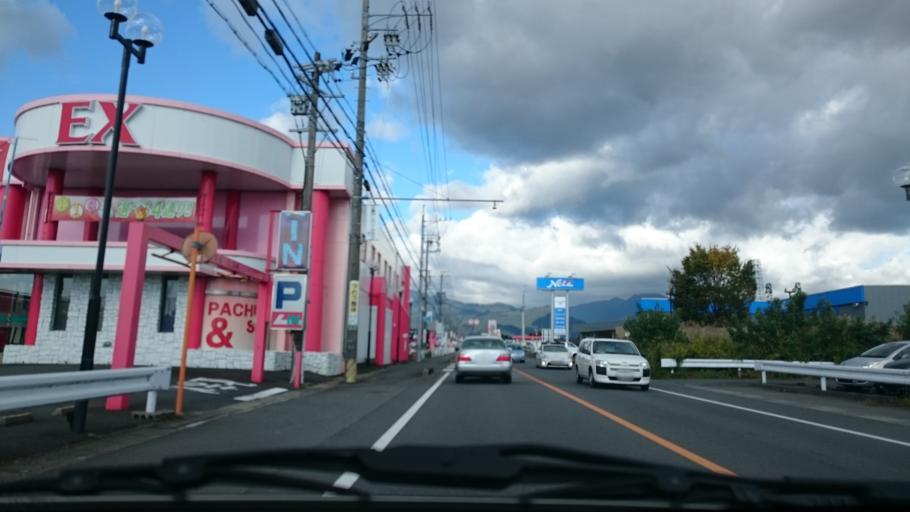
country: JP
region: Mie
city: Komono
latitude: 35.0019
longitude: 136.5345
